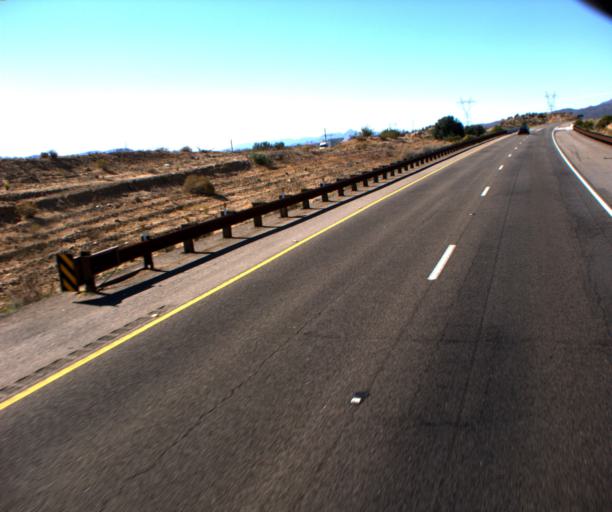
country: US
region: Arizona
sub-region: Yavapai County
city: Bagdad
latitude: 34.7552
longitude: -113.6165
